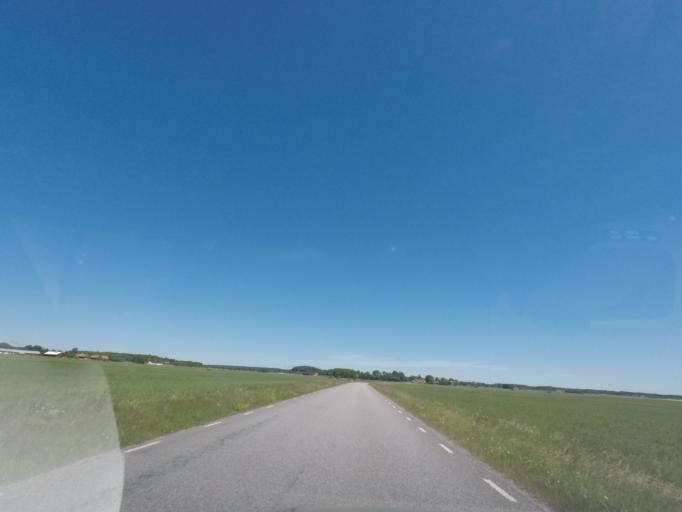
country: SE
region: Uppsala
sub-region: Enkopings Kommun
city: Irsta
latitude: 59.6892
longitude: 16.9637
